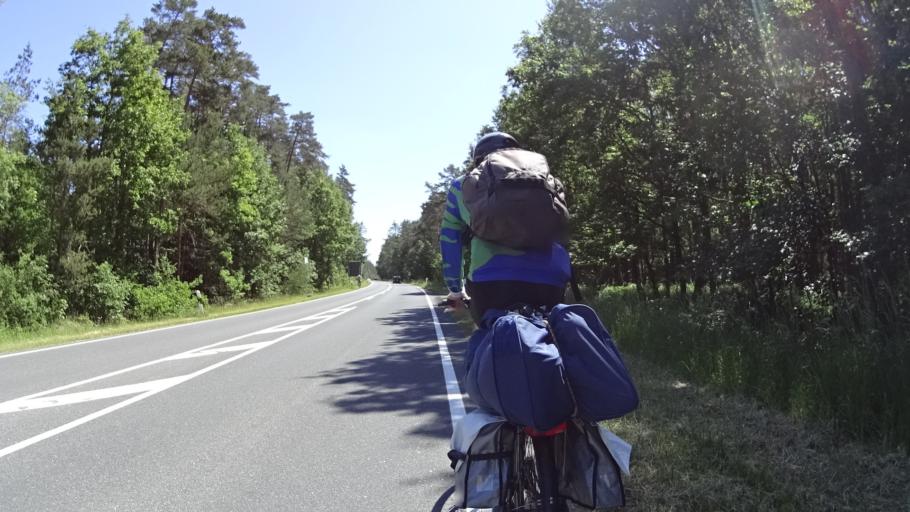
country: DE
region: Bavaria
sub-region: Regierungsbezirk Mittelfranken
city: Pfofeld
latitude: 49.1200
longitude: 10.8201
